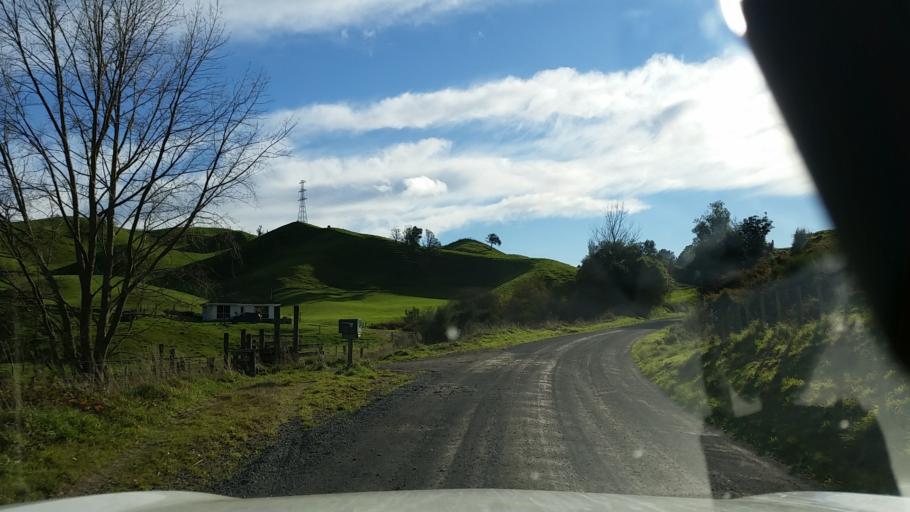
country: NZ
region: Waikato
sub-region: South Waikato District
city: Tokoroa
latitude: -38.3720
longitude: 176.0864
